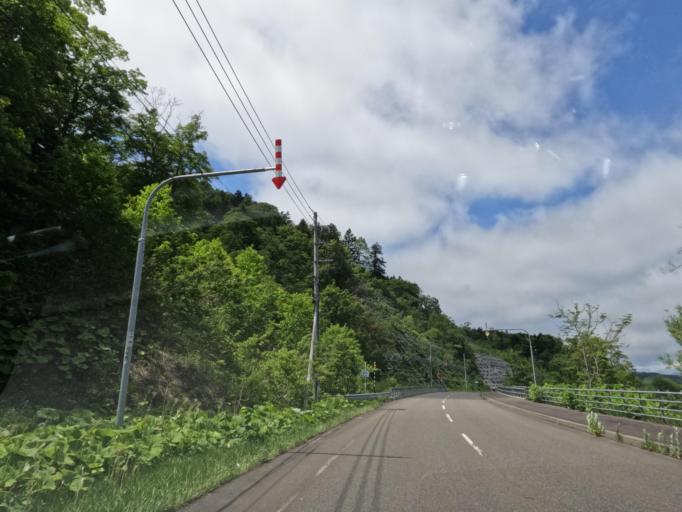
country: JP
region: Hokkaido
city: Tobetsu
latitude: 43.3321
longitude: 141.5690
